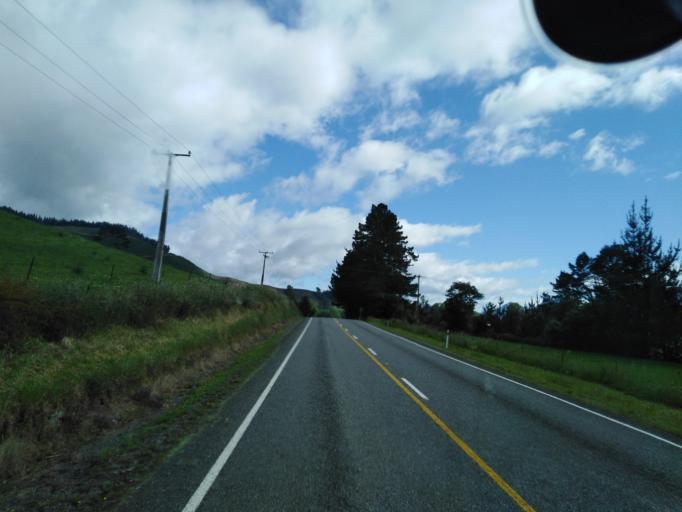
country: NZ
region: Nelson
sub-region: Nelson City
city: Nelson
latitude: -41.2743
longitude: 173.5730
